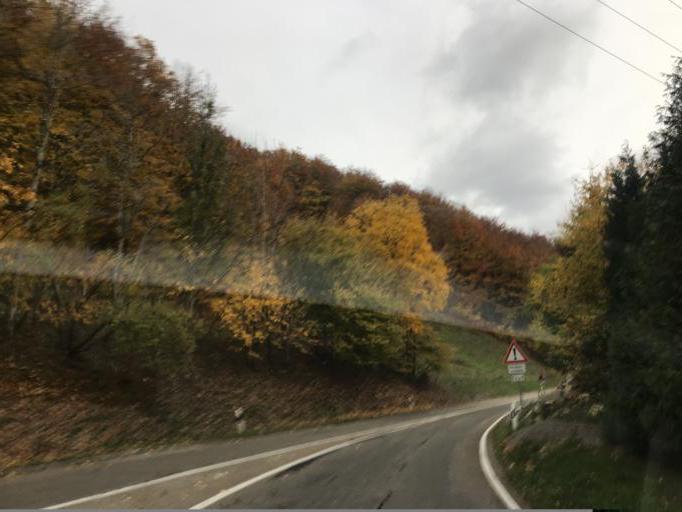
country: DE
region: Baden-Wuerttemberg
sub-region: Freiburg Region
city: Horben
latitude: 47.8836
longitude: 7.8458
